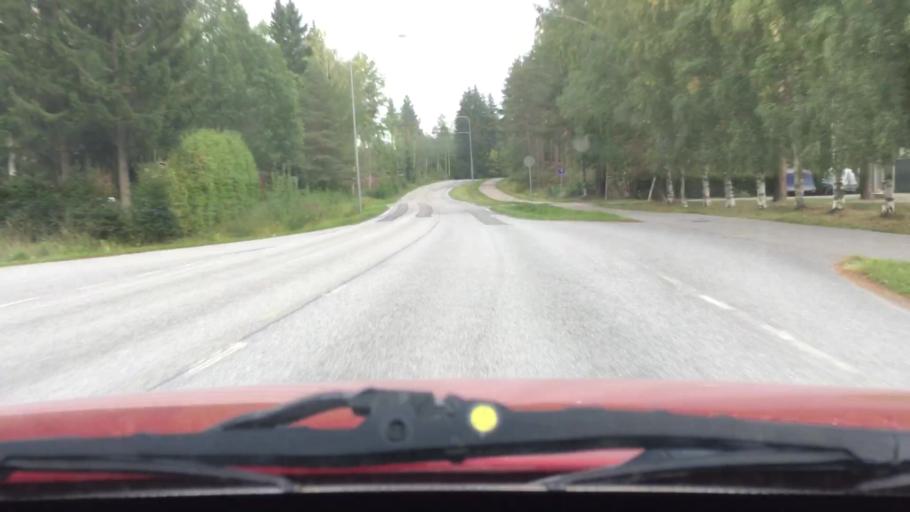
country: FI
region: Varsinais-Suomi
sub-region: Turku
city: Masku
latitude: 60.5555
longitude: 22.1288
